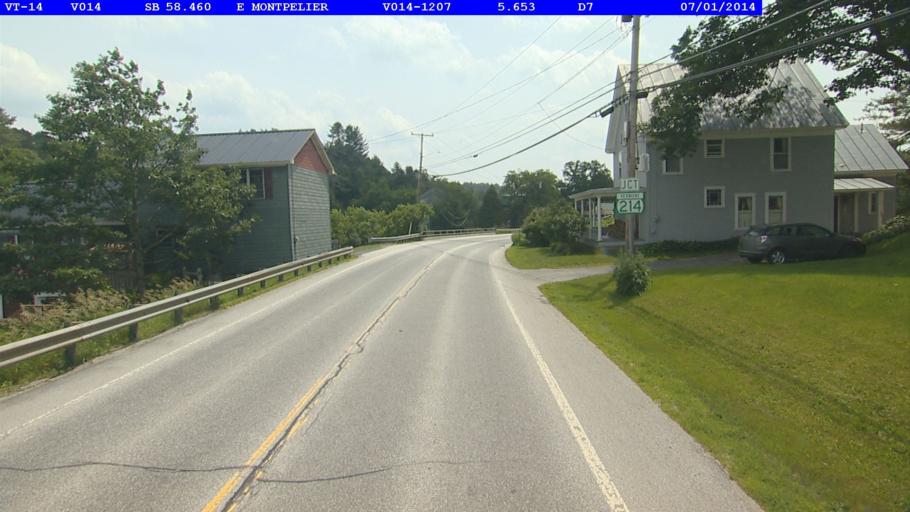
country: US
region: Vermont
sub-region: Washington County
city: Barre
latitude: 44.3055
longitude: -72.4465
